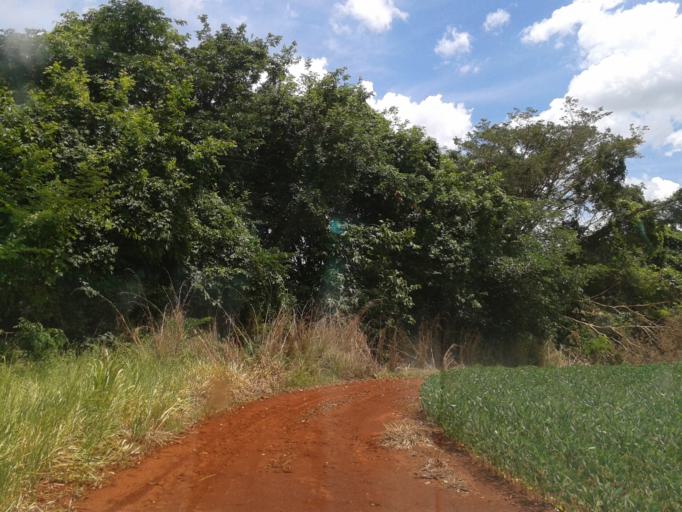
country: BR
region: Minas Gerais
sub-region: Centralina
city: Centralina
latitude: -18.6818
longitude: -49.2166
